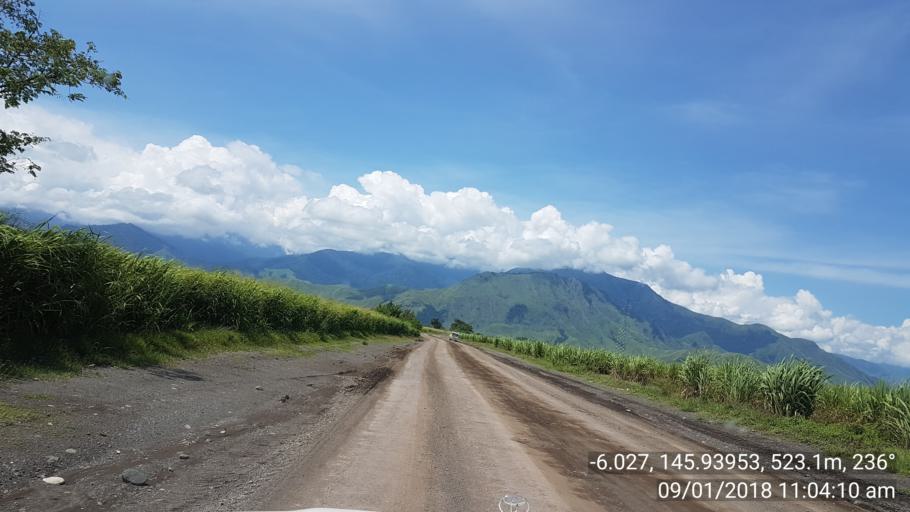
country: PG
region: Eastern Highlands
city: Kainantu
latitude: -6.0270
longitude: 145.9396
